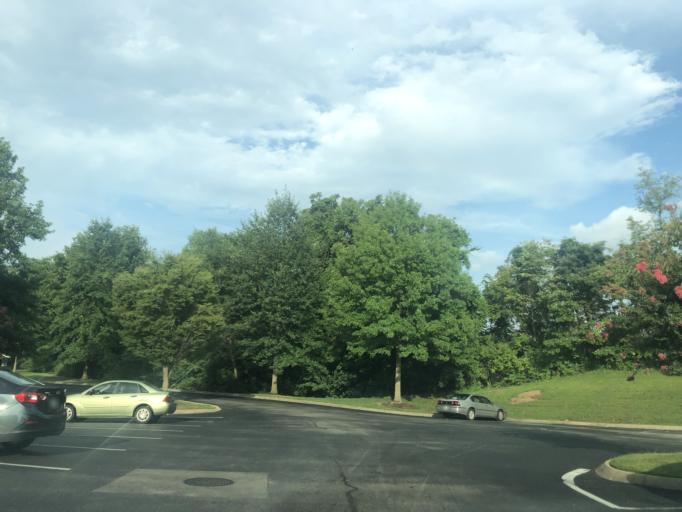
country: US
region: Tennessee
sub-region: Davidson County
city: Lakewood
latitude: 36.1686
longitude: -86.6101
